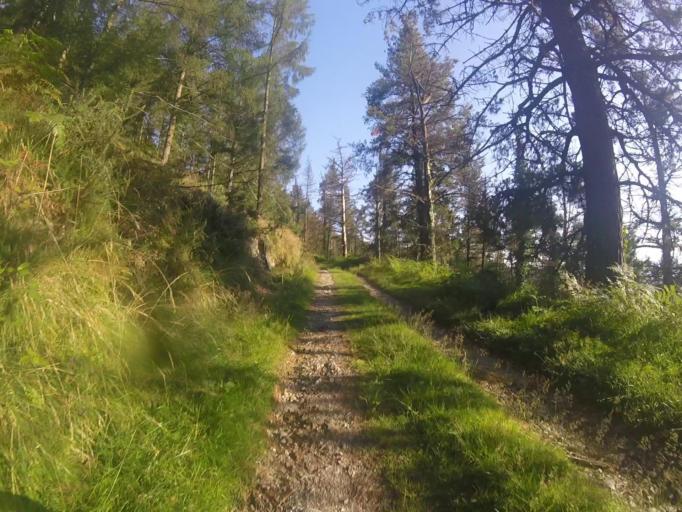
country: ES
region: Navarre
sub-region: Provincia de Navarra
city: Arano
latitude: 43.2484
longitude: -1.8523
